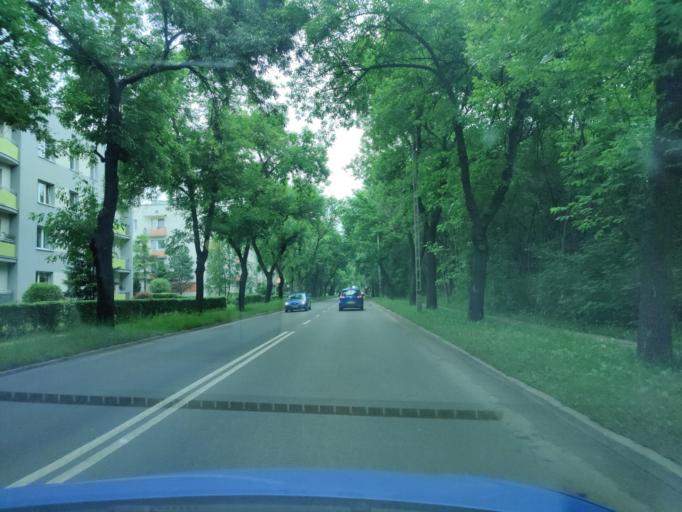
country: PL
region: Silesian Voivodeship
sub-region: Sosnowiec
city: Sosnowiec
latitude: 50.2700
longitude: 19.1471
